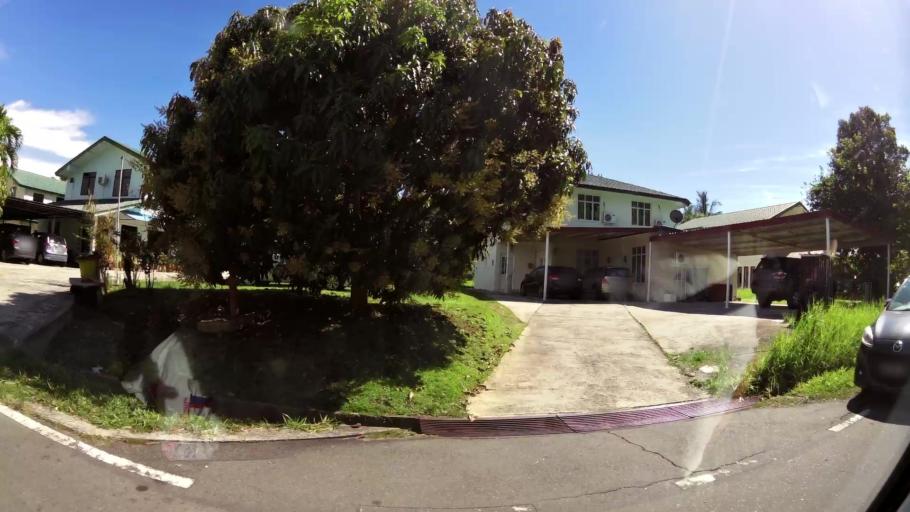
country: BN
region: Brunei and Muara
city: Bandar Seri Begawan
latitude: 5.0036
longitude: 115.0474
